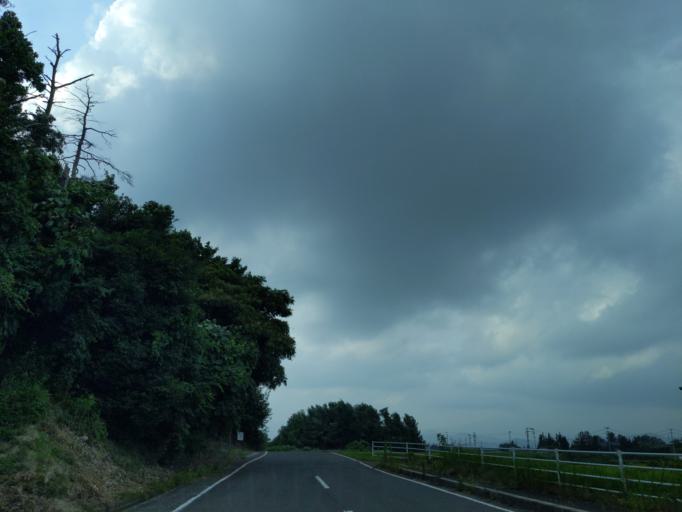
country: JP
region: Fukushima
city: Koriyama
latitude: 37.4337
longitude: 140.3723
